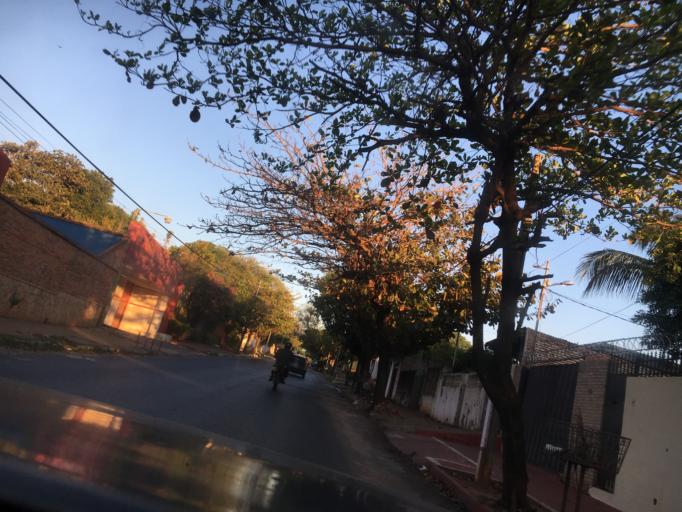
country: PY
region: Asuncion
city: Asuncion
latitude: -25.3172
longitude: -57.6159
